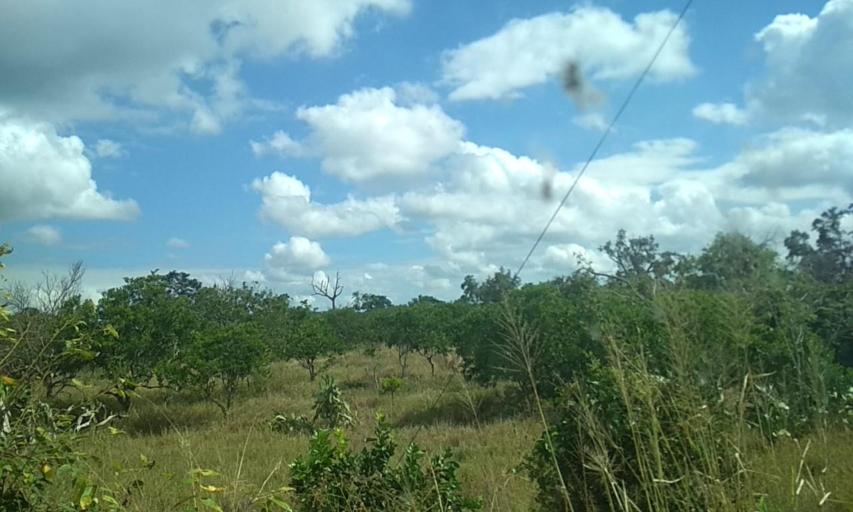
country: MX
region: Puebla
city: San Jose Acateno
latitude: 20.2774
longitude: -97.1316
